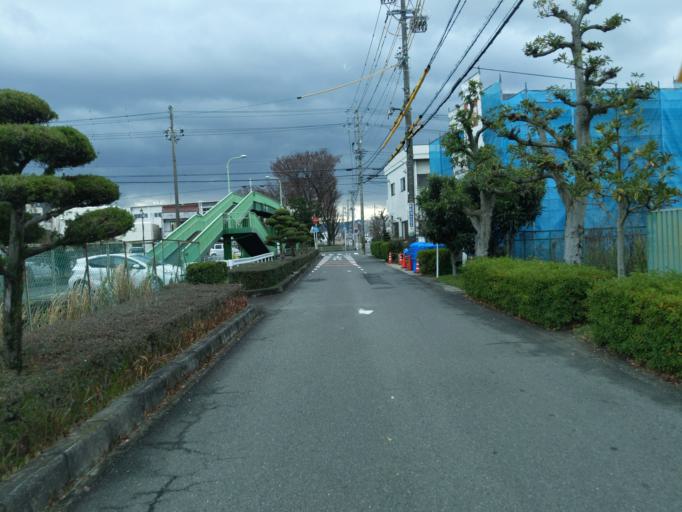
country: JP
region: Aichi
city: Kasugai
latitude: 35.2560
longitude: 136.9889
